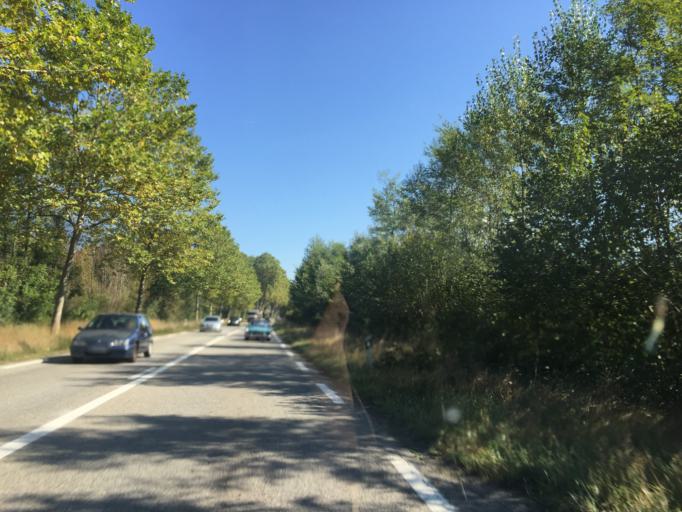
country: FR
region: Rhone-Alpes
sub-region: Departement de la Savoie
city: Coise-Saint-Jean-Pied-Gauthier
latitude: 45.5473
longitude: 6.1468
